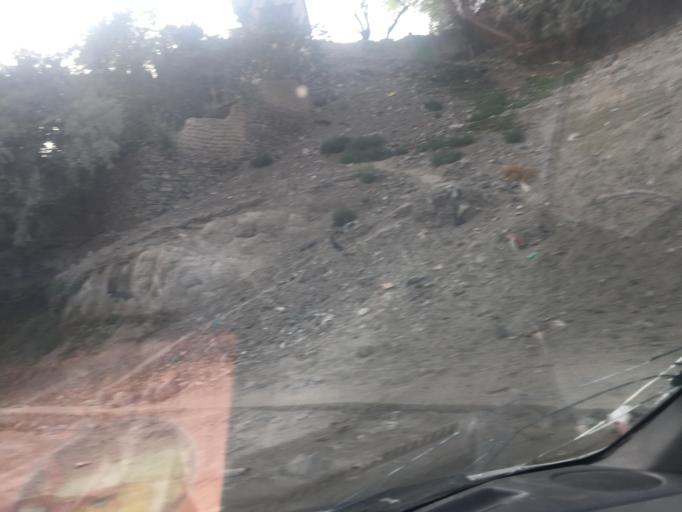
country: PK
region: Gilgit-Baltistan
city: Skardu
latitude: 35.3003
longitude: 75.6279
